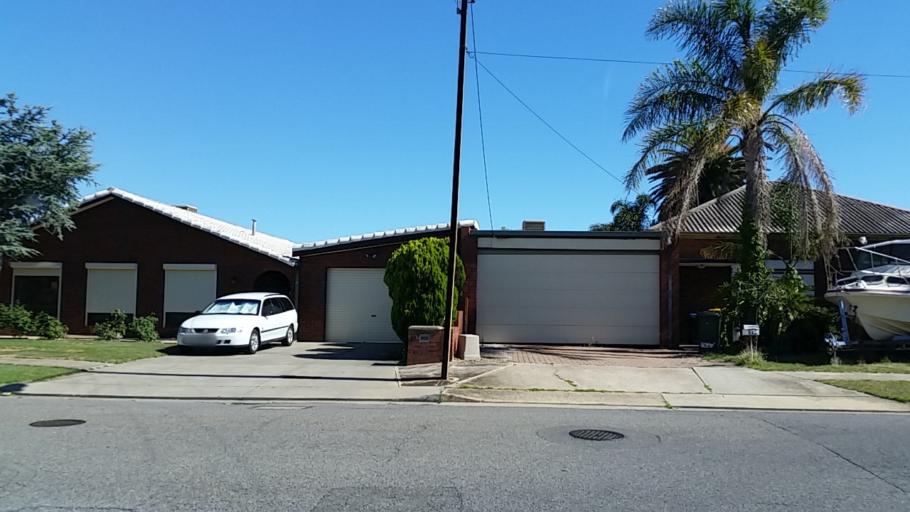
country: AU
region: South Australia
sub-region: Charles Sturt
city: Royal Park
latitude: -34.8879
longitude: 138.5065
